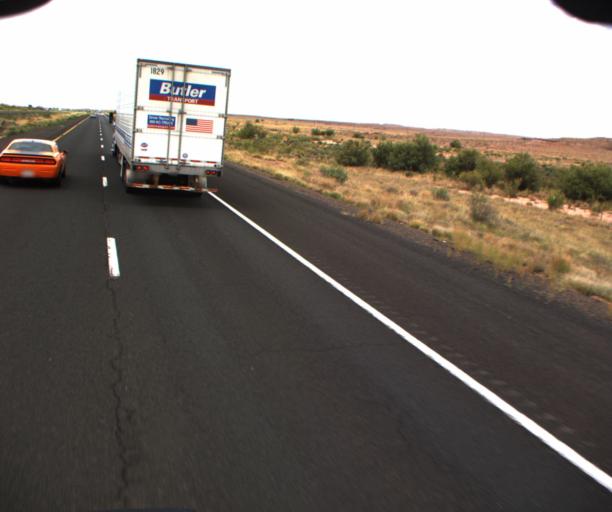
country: US
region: Arizona
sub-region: Navajo County
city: Joseph City
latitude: 34.9707
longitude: -110.4545
